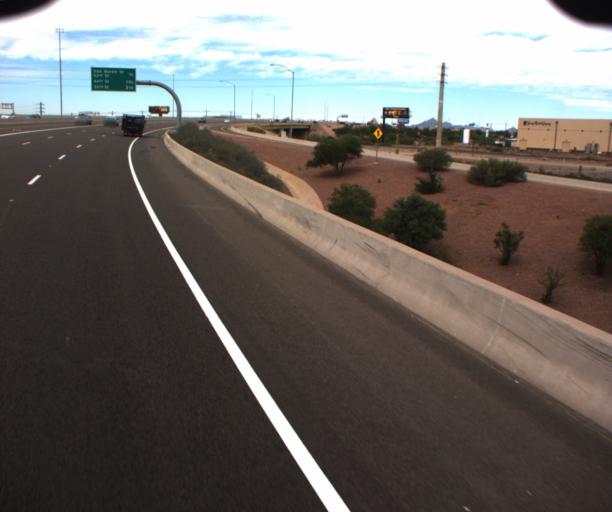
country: US
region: Arizona
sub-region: Maricopa County
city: Tempe Junction
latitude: 33.4395
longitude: -111.9661
